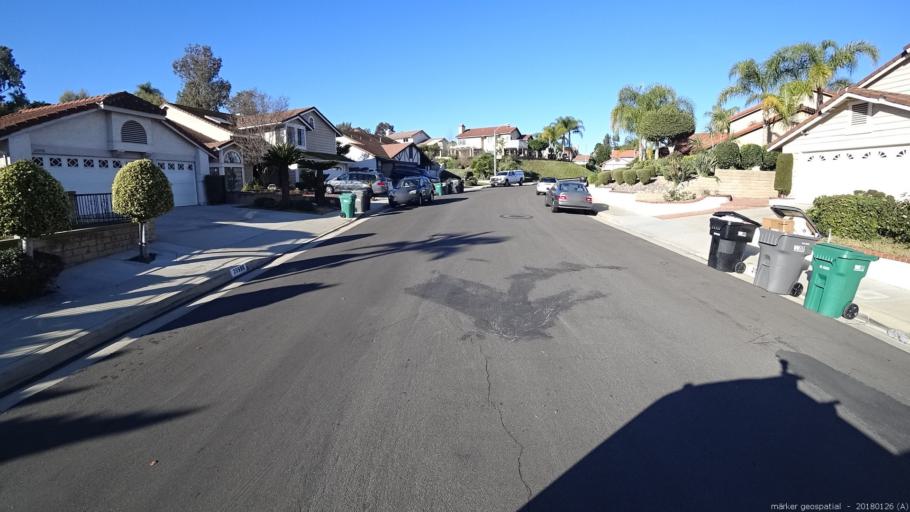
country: US
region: California
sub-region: Los Angeles County
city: Walnut
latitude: 33.9866
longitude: -117.8487
